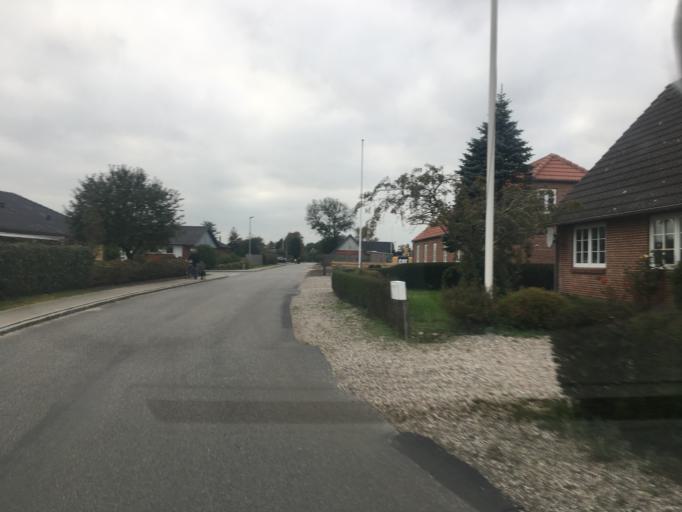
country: DK
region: South Denmark
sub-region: Tonder Kommune
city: Tonder
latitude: 54.9801
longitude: 8.8764
